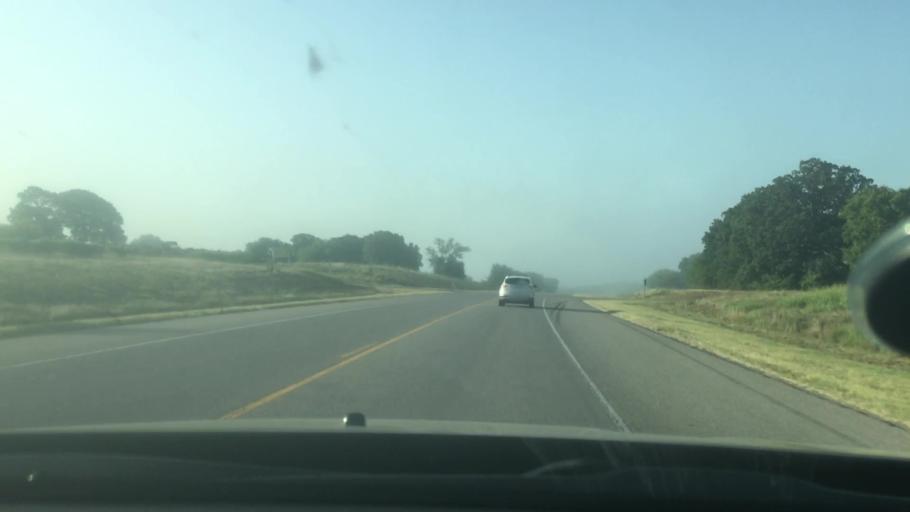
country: US
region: Oklahoma
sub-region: Pontotoc County
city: Ada
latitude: 34.6955
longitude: -96.5979
